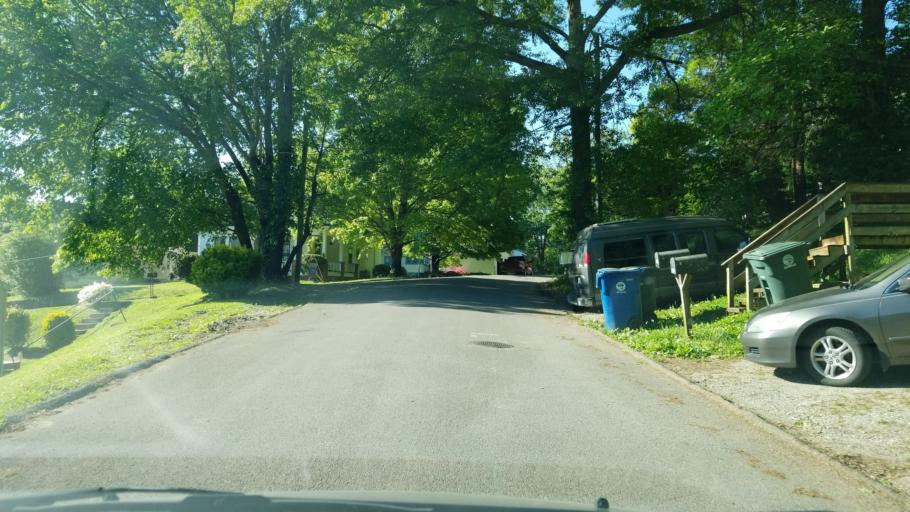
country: US
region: Tennessee
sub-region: Hamilton County
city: Lookout Mountain
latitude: 34.9920
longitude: -85.3328
